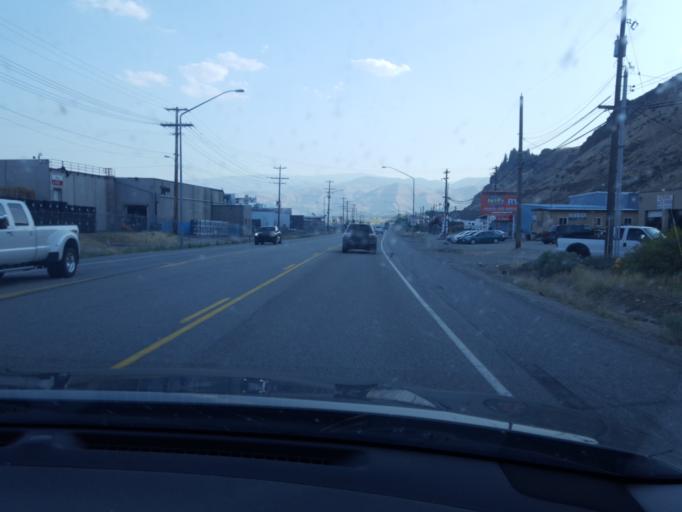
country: US
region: Washington
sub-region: Chelan County
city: Sunnyslope
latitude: 47.4879
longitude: -120.3161
